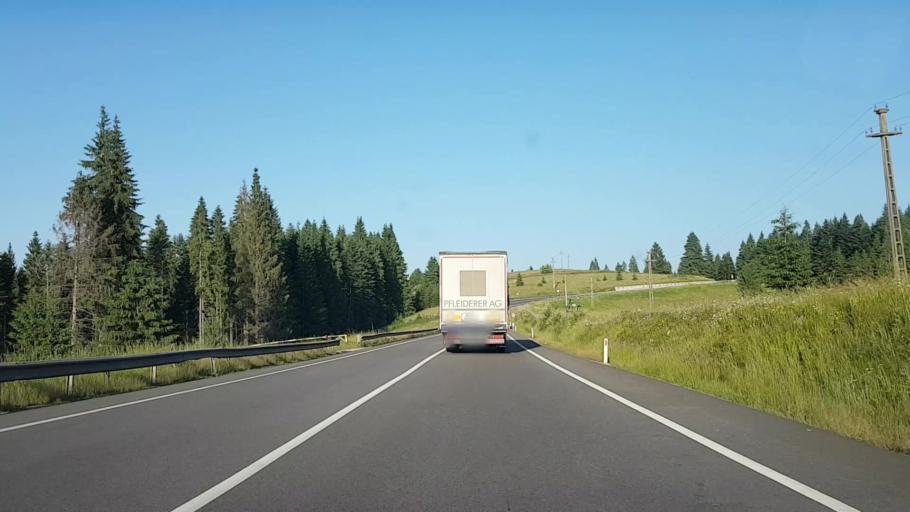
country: RO
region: Suceava
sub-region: Comuna Poiana Stampei
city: Poiana Stampei
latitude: 47.2870
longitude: 25.0635
